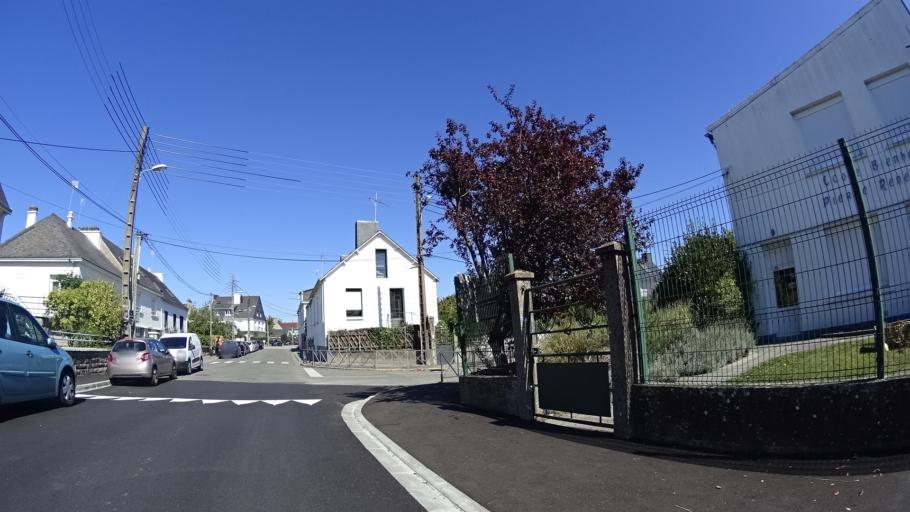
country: FR
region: Brittany
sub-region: Departement du Morbihan
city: Vannes
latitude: 47.6434
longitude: -2.7653
